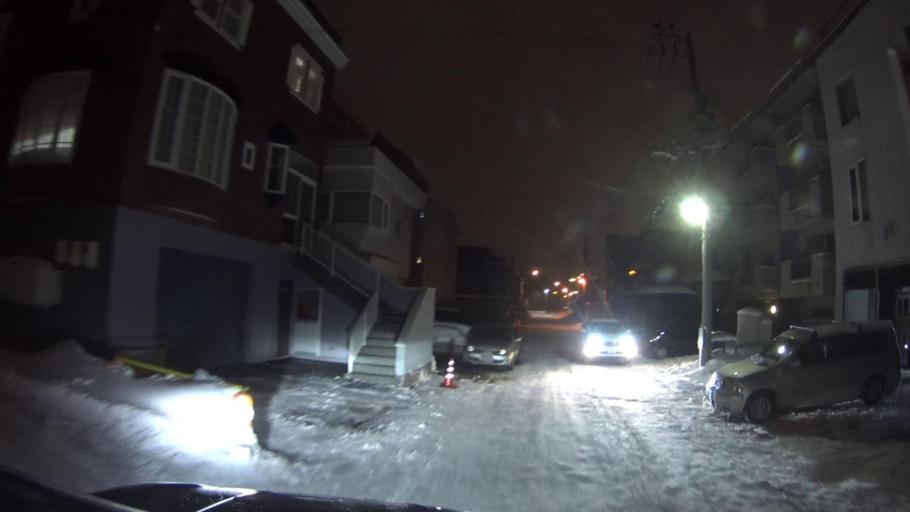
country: JP
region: Hokkaido
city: Sapporo
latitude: 43.0933
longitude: 141.2744
